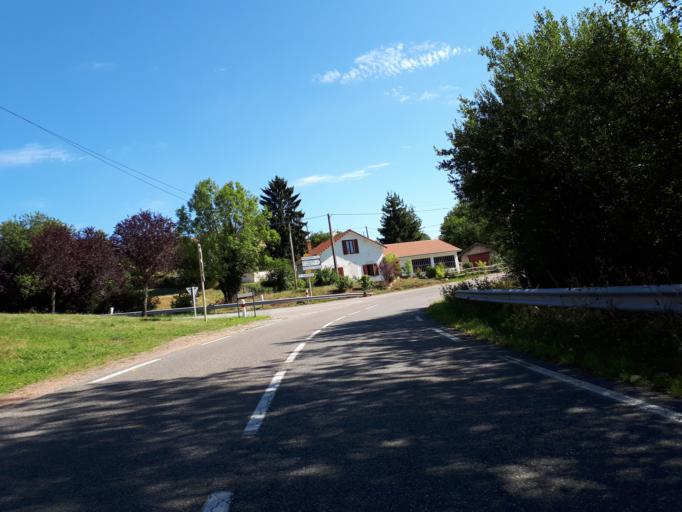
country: FR
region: Rhone-Alpes
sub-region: Departement de la Loire
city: Bussieres
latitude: 45.8394
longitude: 4.2662
